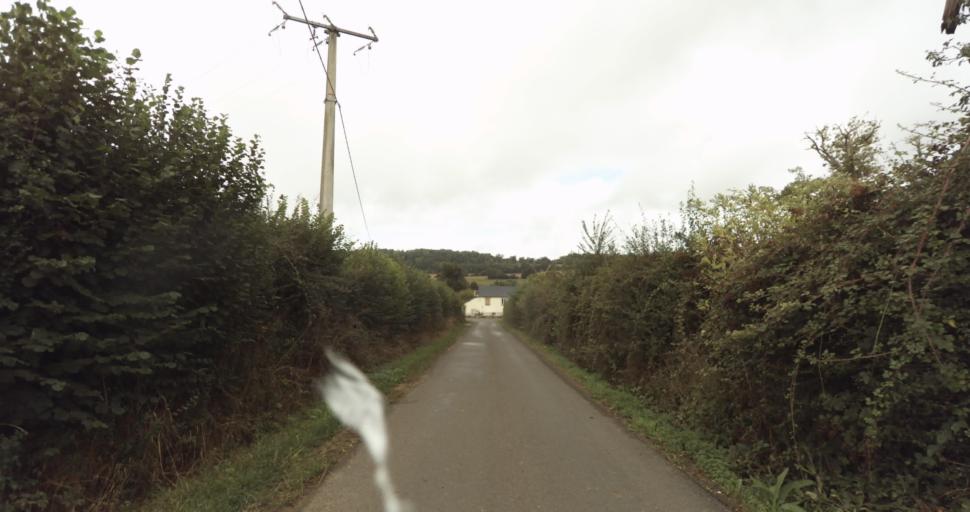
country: FR
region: Lower Normandy
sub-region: Departement de l'Orne
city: Gace
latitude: 48.8690
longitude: 0.2806
